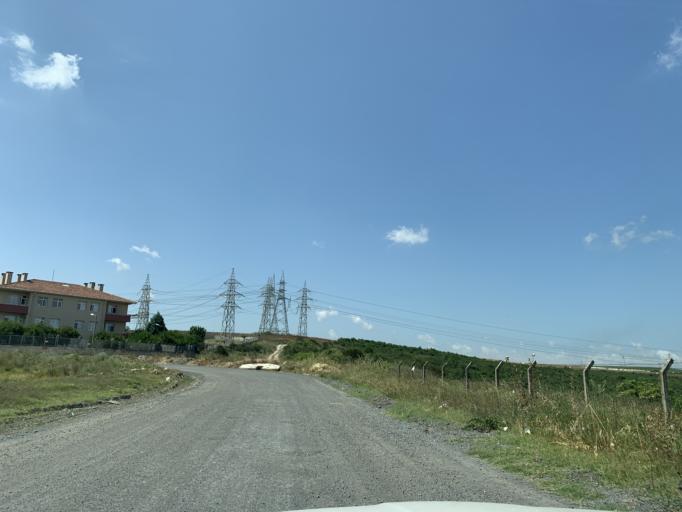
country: TR
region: Istanbul
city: Esenyurt
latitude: 41.0874
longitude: 28.6927
